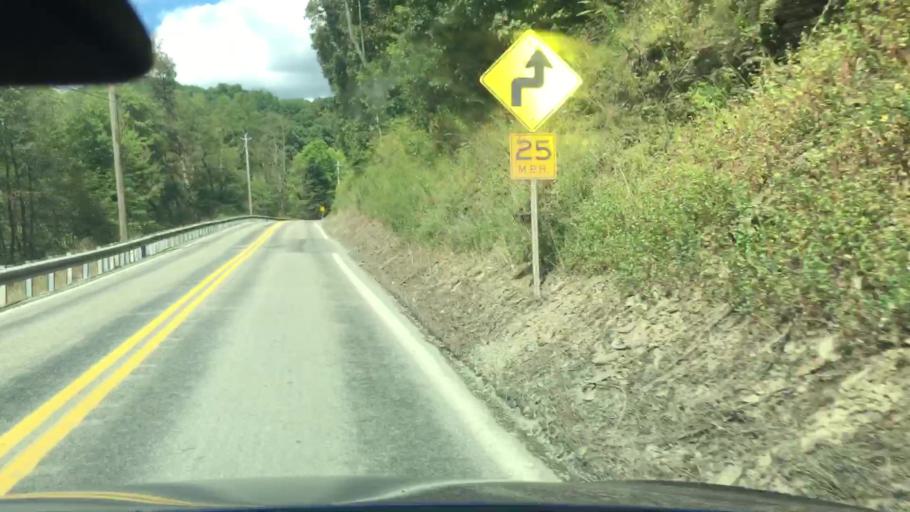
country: US
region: Pennsylvania
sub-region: Allegheny County
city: Curtisville
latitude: 40.6427
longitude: -79.8397
